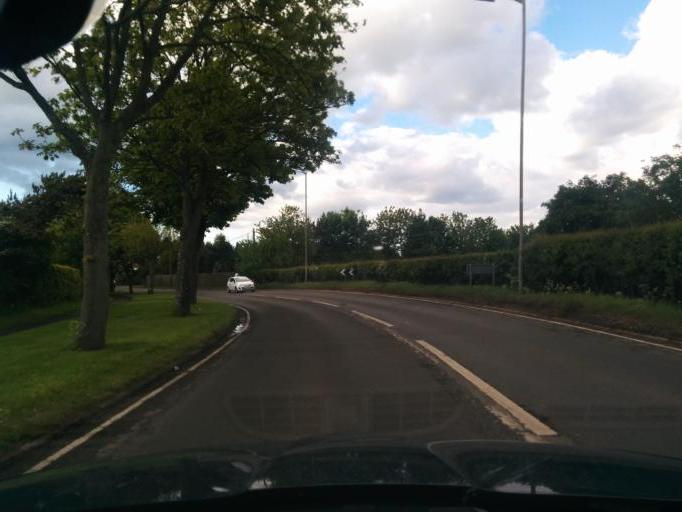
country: GB
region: England
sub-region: Northumberland
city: Bedlington
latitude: 55.1389
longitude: -1.5982
